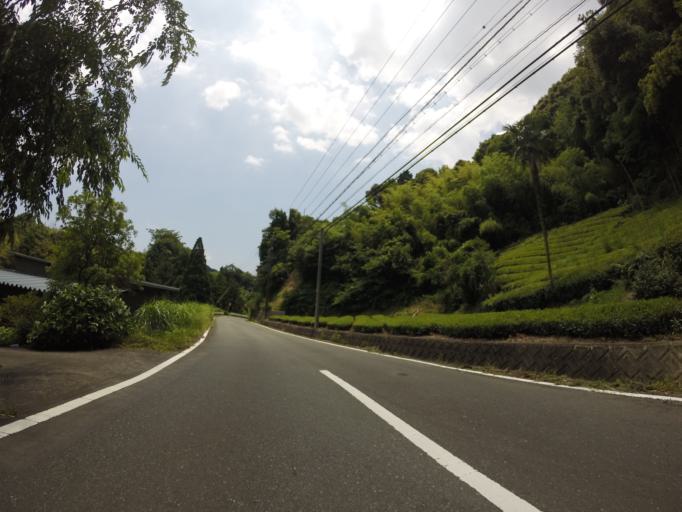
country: JP
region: Shizuoka
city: Kanaya
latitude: 34.8335
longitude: 138.0743
